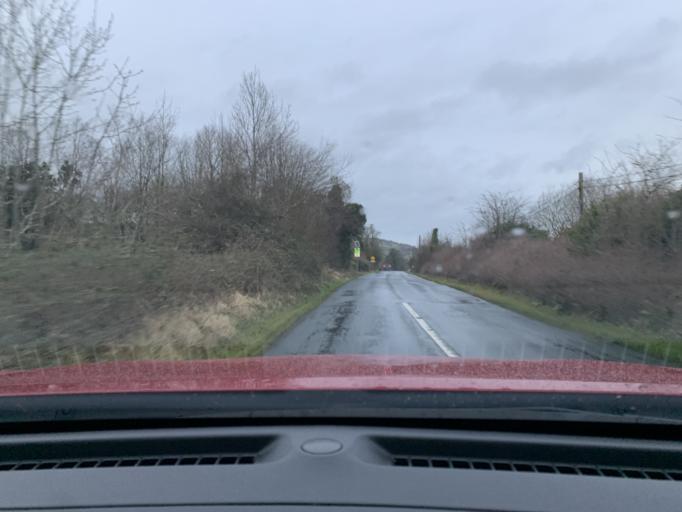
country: IE
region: Connaught
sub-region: Roscommon
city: Boyle
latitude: 54.0231
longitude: -8.3285
